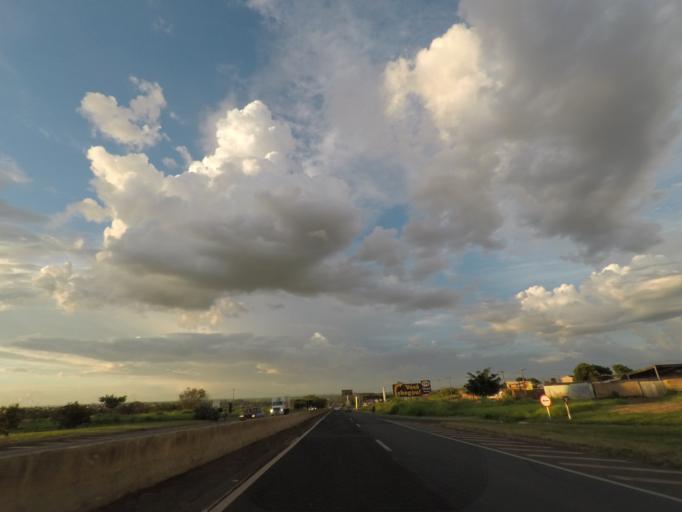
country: BR
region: Minas Gerais
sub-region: Uberaba
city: Uberaba
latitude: -19.7700
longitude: -47.9741
